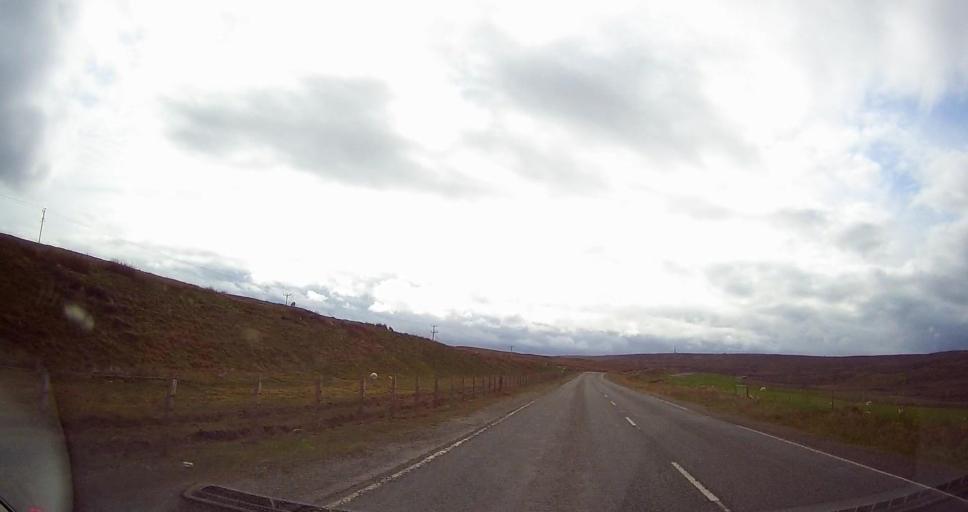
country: GB
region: Scotland
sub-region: Shetland Islands
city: Lerwick
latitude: 60.4448
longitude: -1.2440
